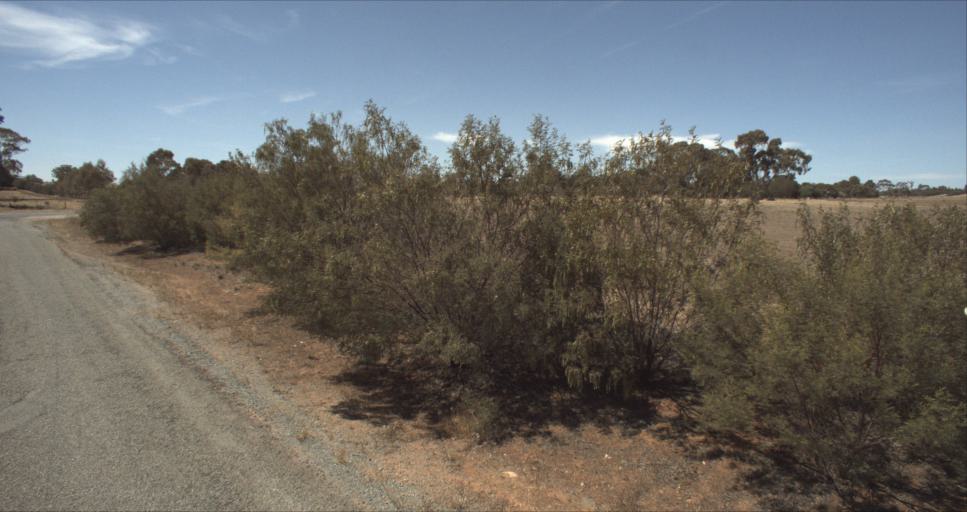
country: AU
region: New South Wales
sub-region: Leeton
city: Leeton
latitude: -34.5891
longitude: 146.4412
